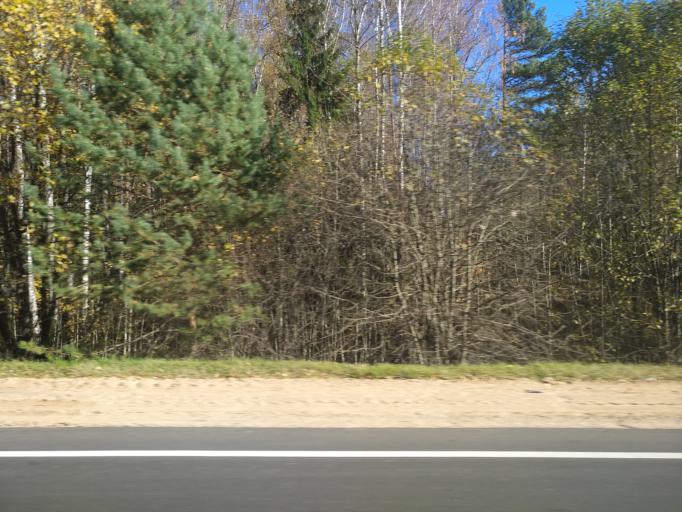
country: BY
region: Minsk
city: Kryvichy
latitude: 54.5896
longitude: 27.1935
